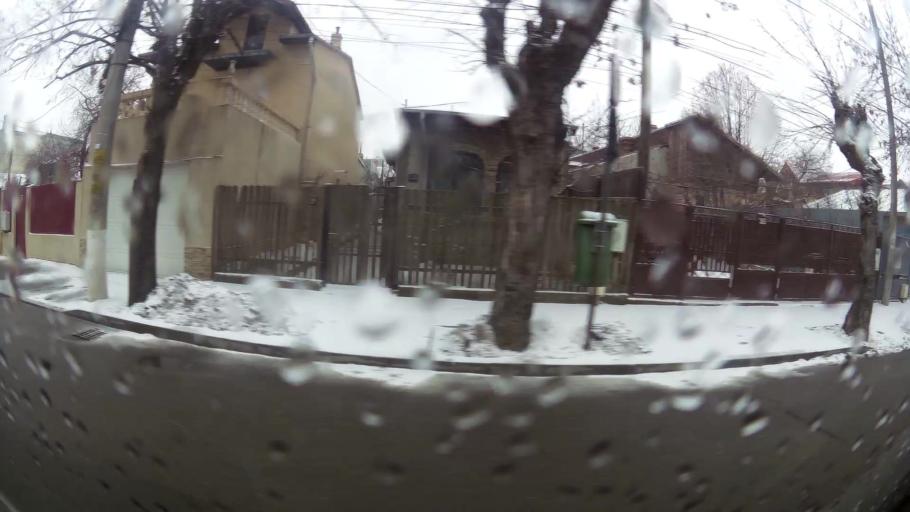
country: RO
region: Prahova
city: Ploiesti
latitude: 44.9441
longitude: 26.0071
